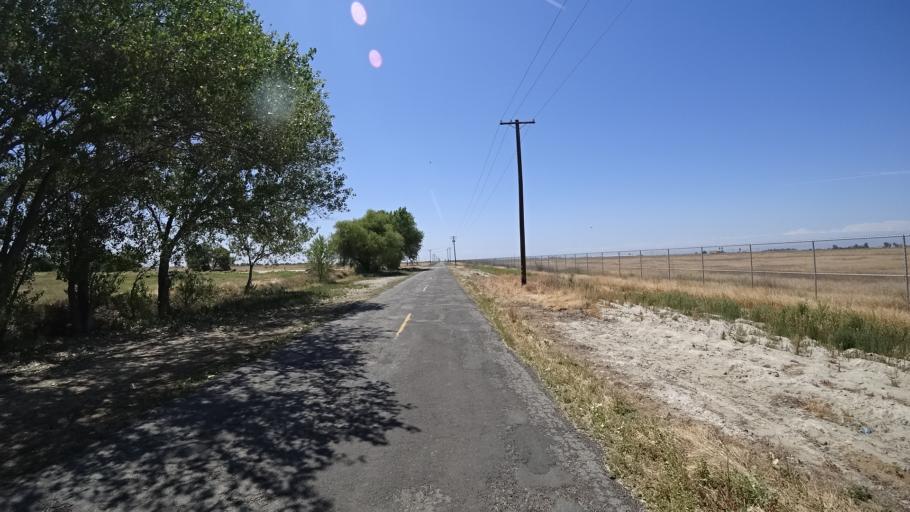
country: US
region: California
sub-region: Kings County
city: Lemoore
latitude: 36.2341
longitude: -119.7447
